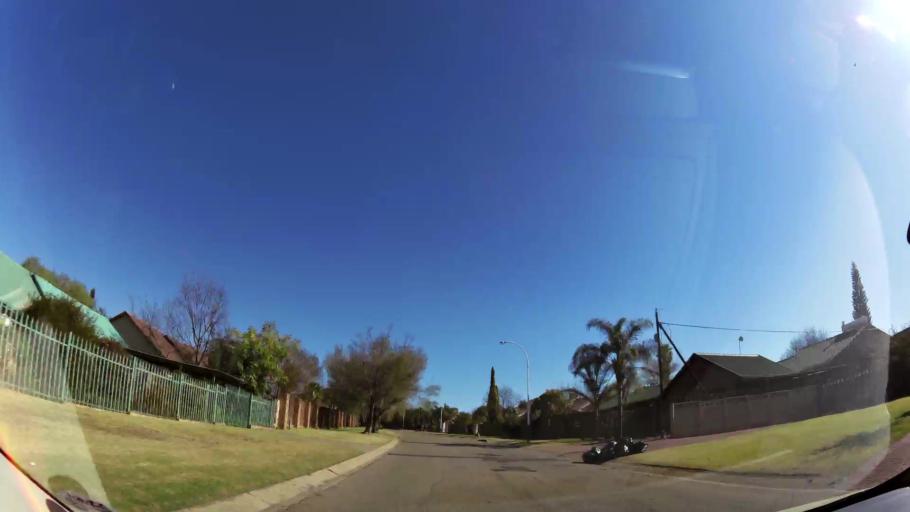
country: ZA
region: Mpumalanga
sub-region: Nkangala District Municipality
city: Witbank
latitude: -25.8712
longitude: 29.2471
